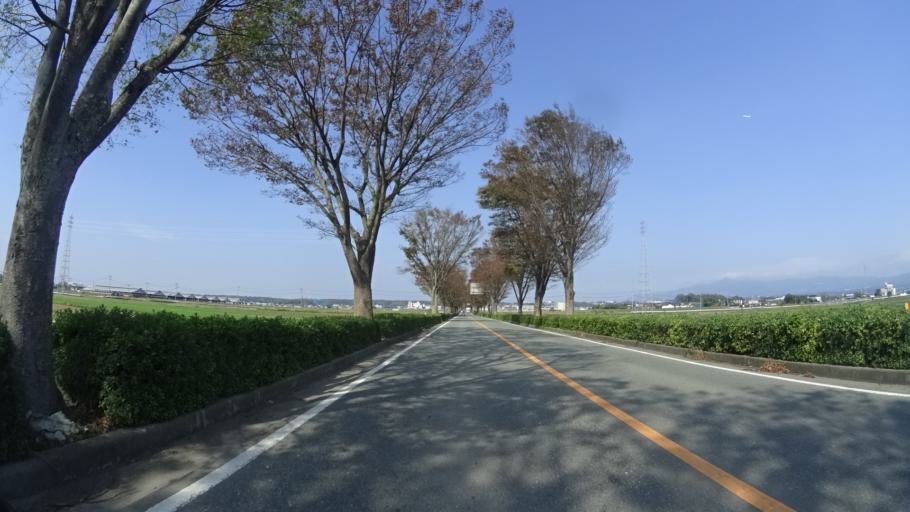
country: JP
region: Kumamoto
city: Ozu
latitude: 32.8595
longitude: 130.8553
